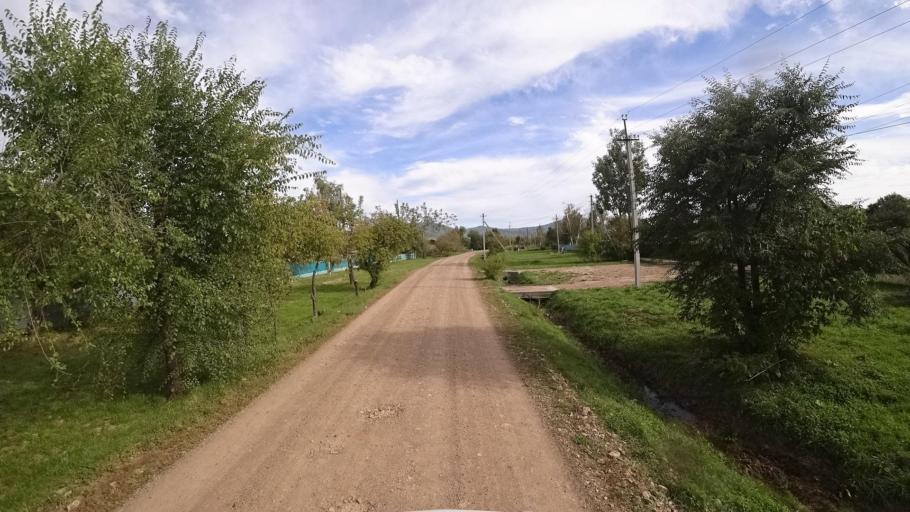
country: RU
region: Primorskiy
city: Dostoyevka
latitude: 44.3053
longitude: 133.4598
